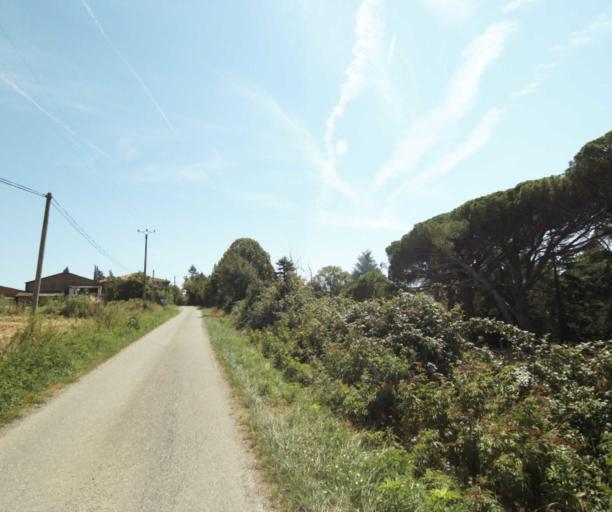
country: FR
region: Midi-Pyrenees
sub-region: Departement de l'Ariege
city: Lezat-sur-Leze
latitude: 43.2565
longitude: 1.3168
